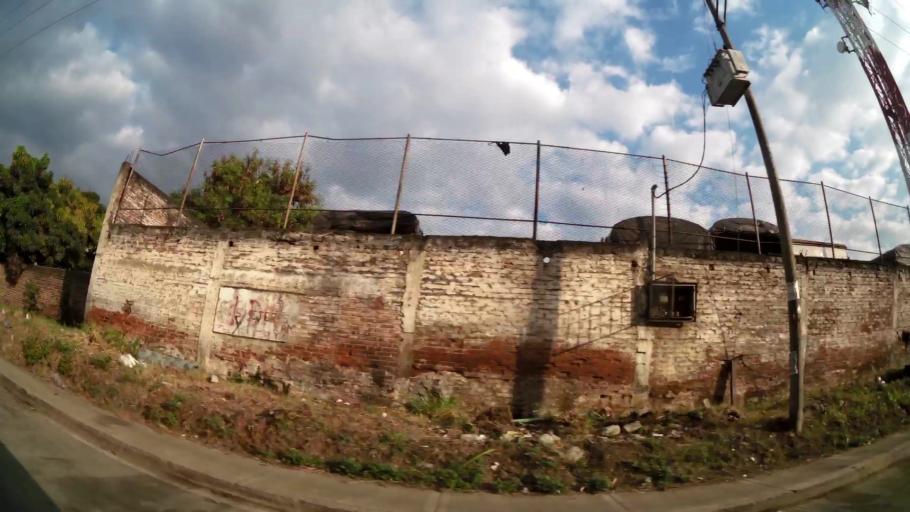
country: CO
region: Valle del Cauca
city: Cali
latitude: 3.4574
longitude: -76.5133
